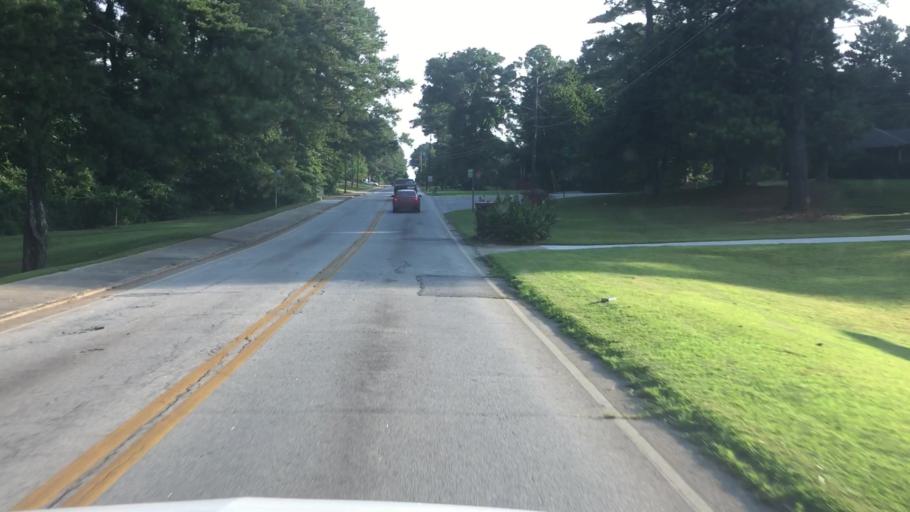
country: US
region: Georgia
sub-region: DeKalb County
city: Panthersville
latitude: 33.7053
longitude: -84.2526
